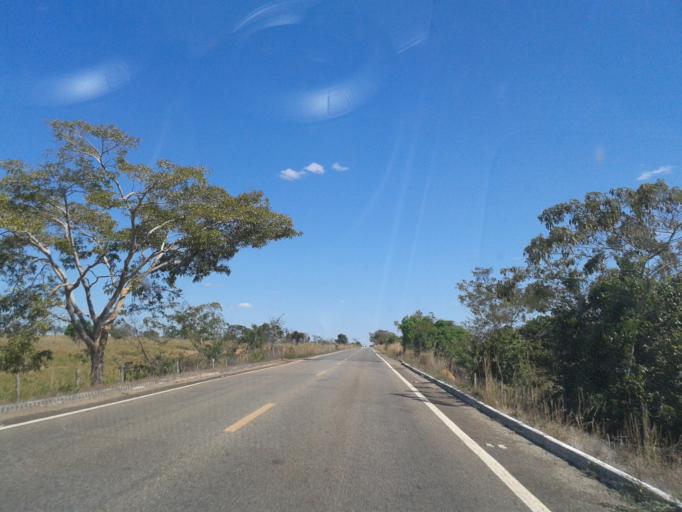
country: BR
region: Goias
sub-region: Sao Miguel Do Araguaia
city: Sao Miguel do Araguaia
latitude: -13.6366
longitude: -50.3141
